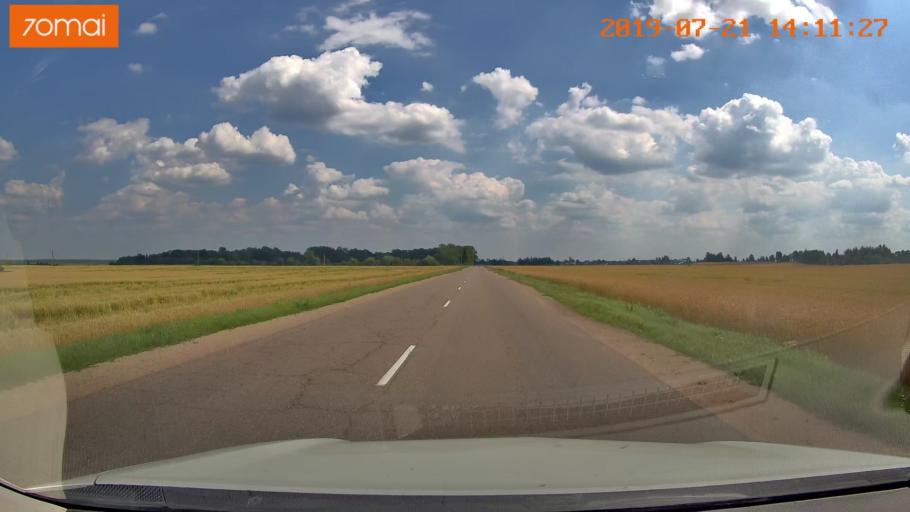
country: BY
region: Grodnenskaya
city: Karelichy
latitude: 53.6575
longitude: 26.1527
